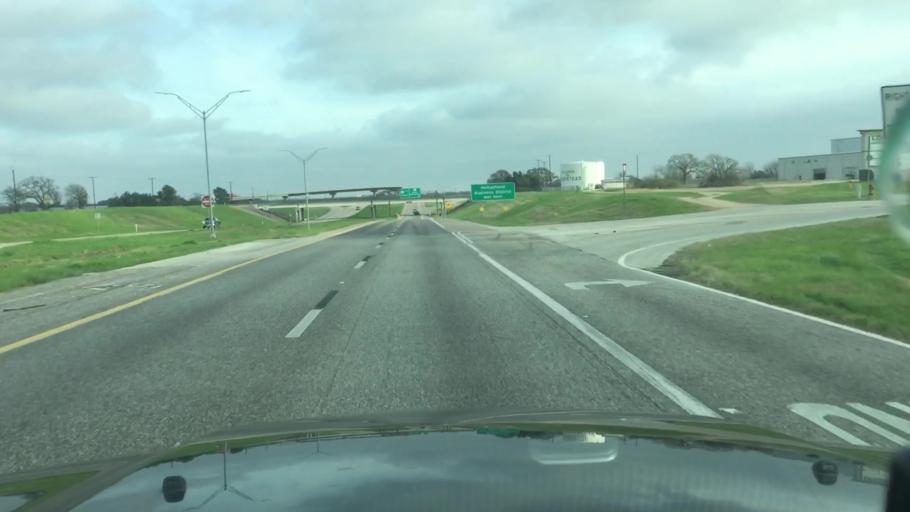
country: US
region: Texas
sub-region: Waller County
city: Hempstead
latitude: 30.1162
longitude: -96.0842
